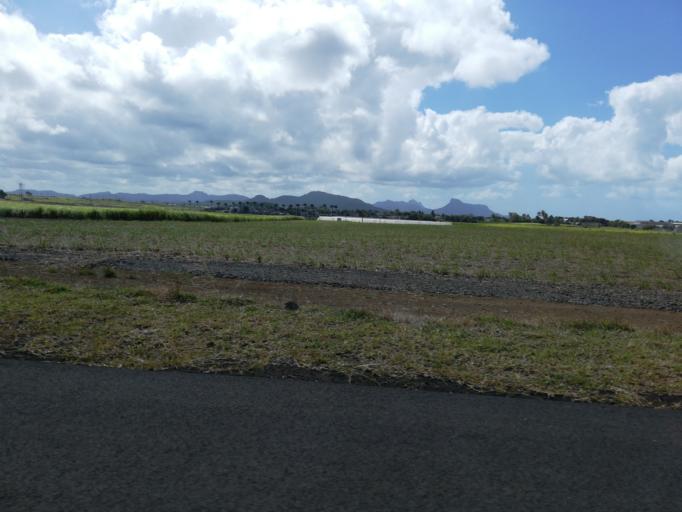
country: MU
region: Grand Port
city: Plaine Magnien
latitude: -20.4372
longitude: 57.6523
